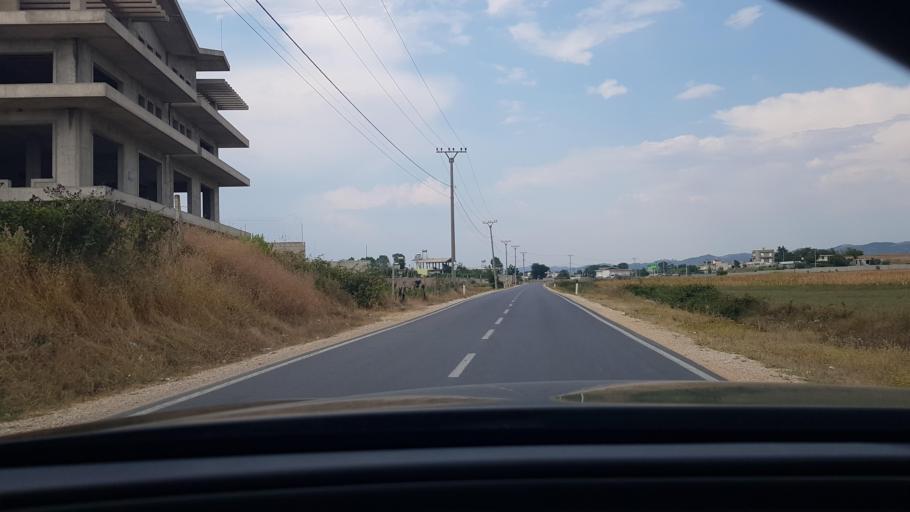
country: AL
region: Durres
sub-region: Rrethi i Durresit
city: Katundi i Ri
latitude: 41.4177
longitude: 19.5467
